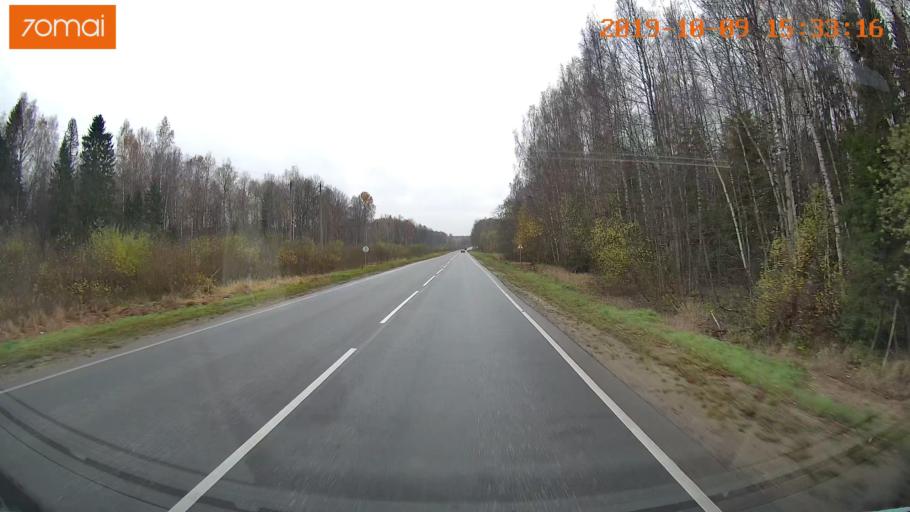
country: RU
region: Kostroma
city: Oktyabr'skiy
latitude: 57.9541
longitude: 41.2648
